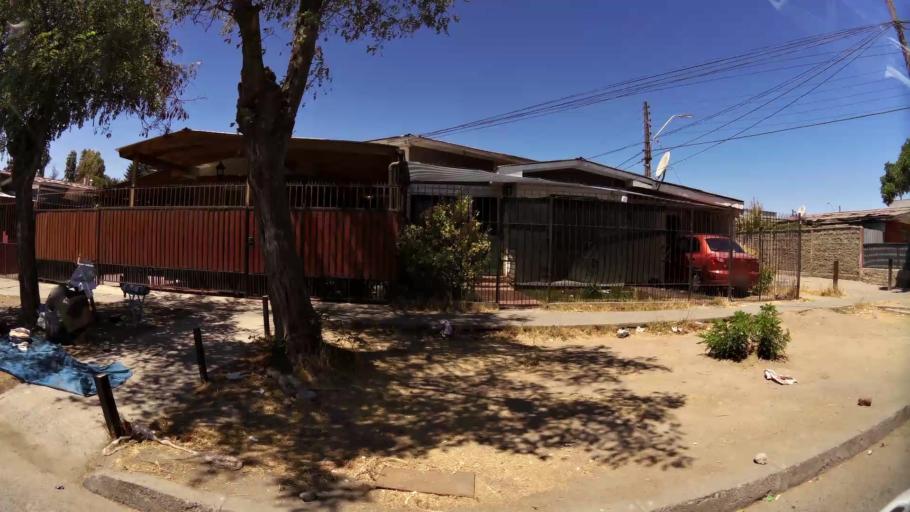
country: CL
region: O'Higgins
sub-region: Provincia de Cachapoal
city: Rancagua
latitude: -34.1664
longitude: -70.7589
